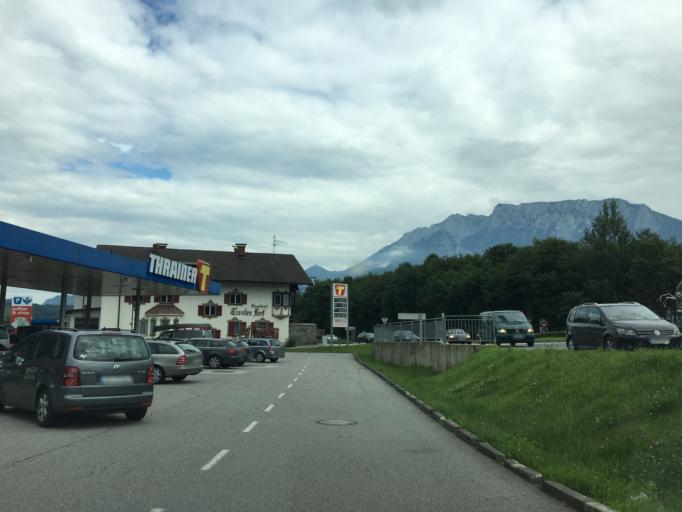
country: AT
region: Tyrol
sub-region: Politischer Bezirk Kufstein
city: Niederndorf
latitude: 47.6487
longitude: 12.1960
